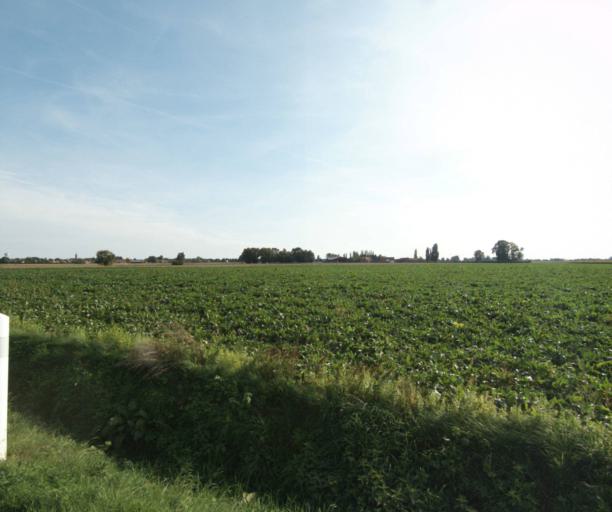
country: FR
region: Nord-Pas-de-Calais
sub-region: Departement du Nord
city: Fournes-en-Weppes
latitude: 50.5956
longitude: 2.8752
